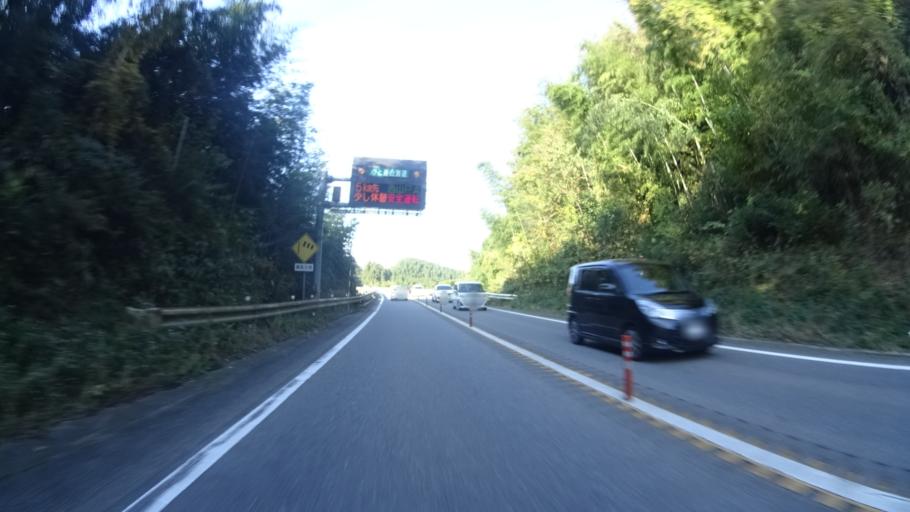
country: JP
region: Ishikawa
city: Hakui
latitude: 36.9729
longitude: 136.8239
